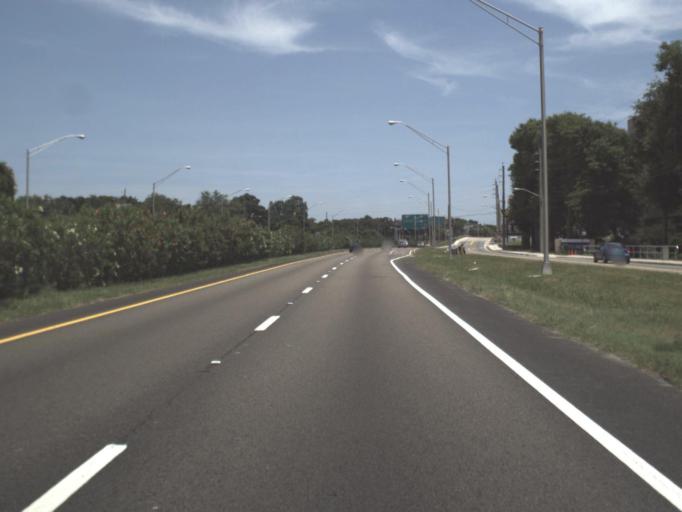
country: US
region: Florida
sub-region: Duval County
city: Jacksonville
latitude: 30.3275
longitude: -81.5750
